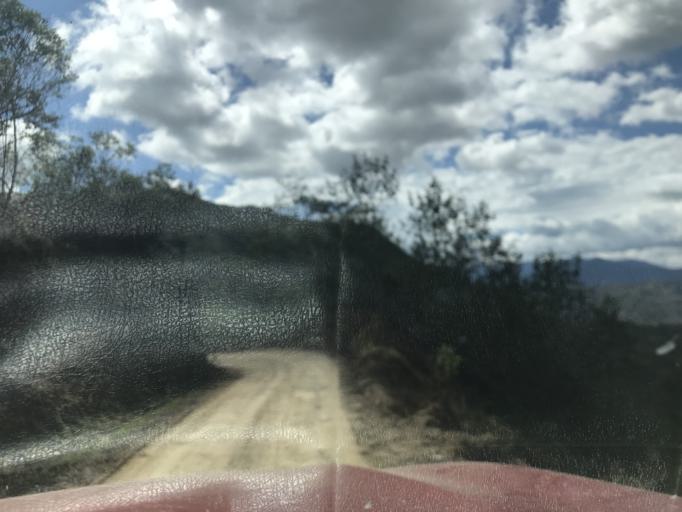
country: PE
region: Cajamarca
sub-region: Provincia de Chota
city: Querocoto
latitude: -6.3475
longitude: -79.0541
